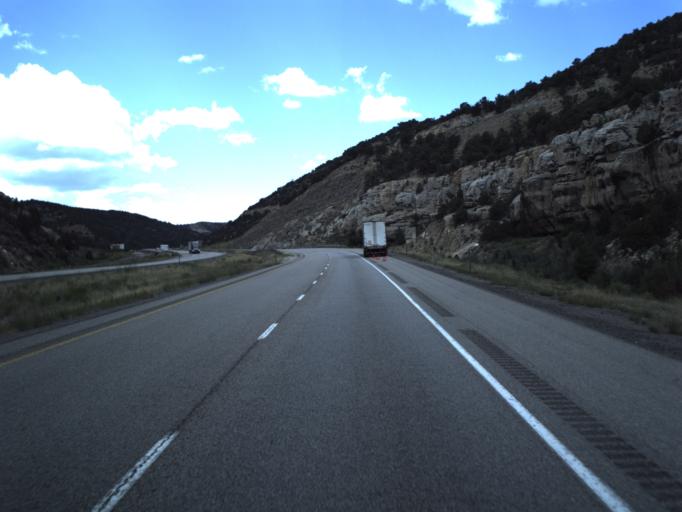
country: US
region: Utah
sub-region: Wayne County
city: Loa
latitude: 38.7585
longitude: -111.4486
